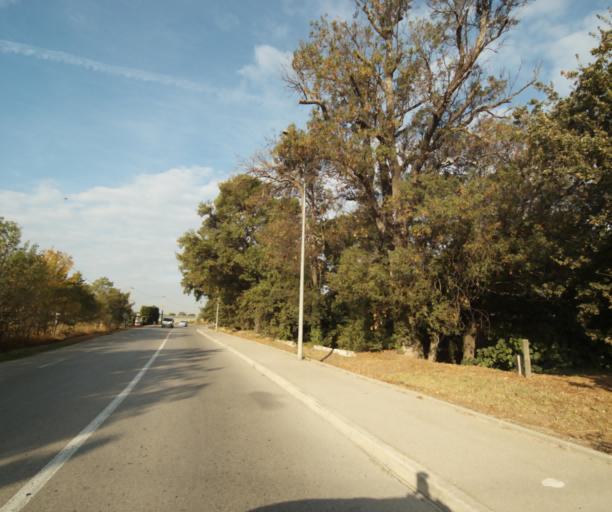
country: FR
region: Provence-Alpes-Cote d'Azur
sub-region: Departement des Bouches-du-Rhone
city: Saint-Victoret
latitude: 43.4161
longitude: 5.2692
